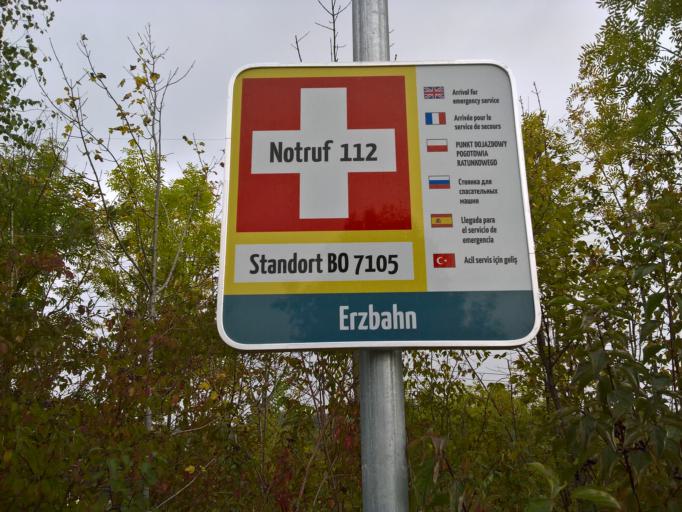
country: DE
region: North Rhine-Westphalia
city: Bochum-Hordel
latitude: 51.5011
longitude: 7.1530
